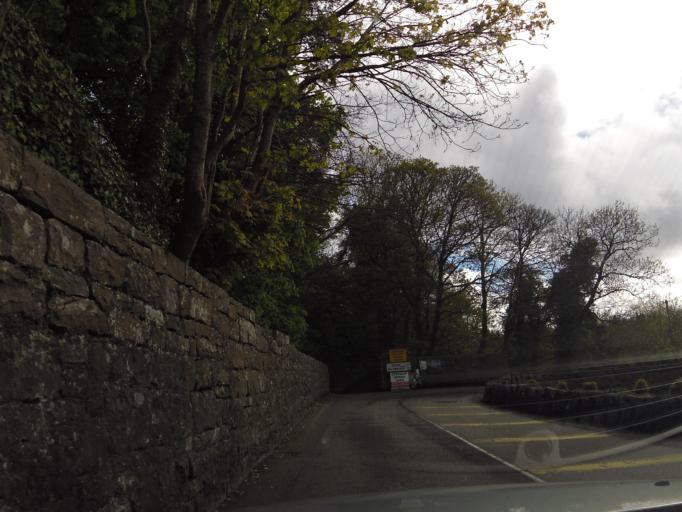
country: IE
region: Connaught
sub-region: Maigh Eo
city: Ballinrobe
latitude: 53.5411
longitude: -9.2841
